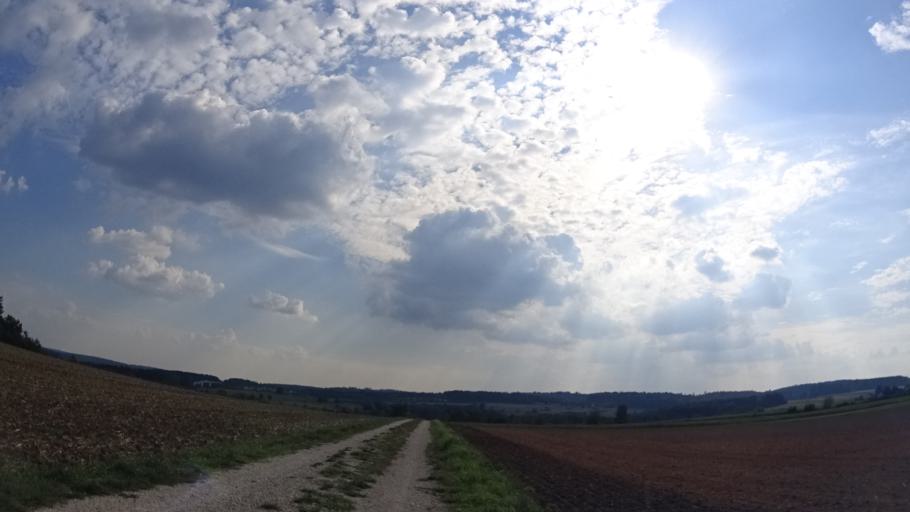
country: DE
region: Bavaria
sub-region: Lower Bavaria
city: Riedenburg
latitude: 48.9655
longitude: 11.6733
